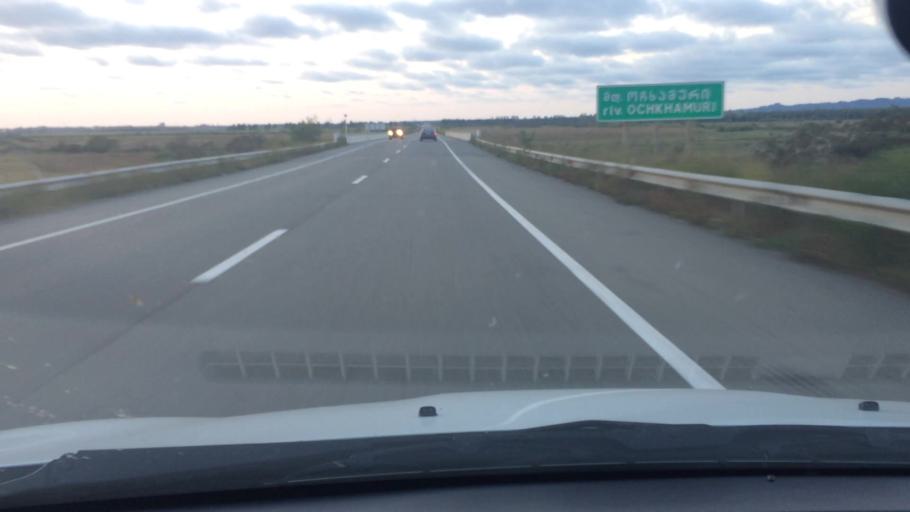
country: GE
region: Ajaria
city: Ochkhamuri
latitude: 41.8705
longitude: 41.8315
